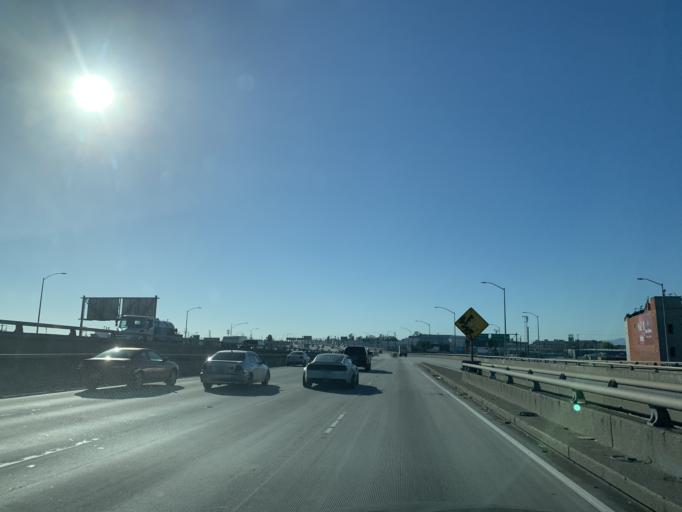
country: US
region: California
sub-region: Los Angeles County
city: Boyle Heights
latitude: 34.0290
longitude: -118.2282
